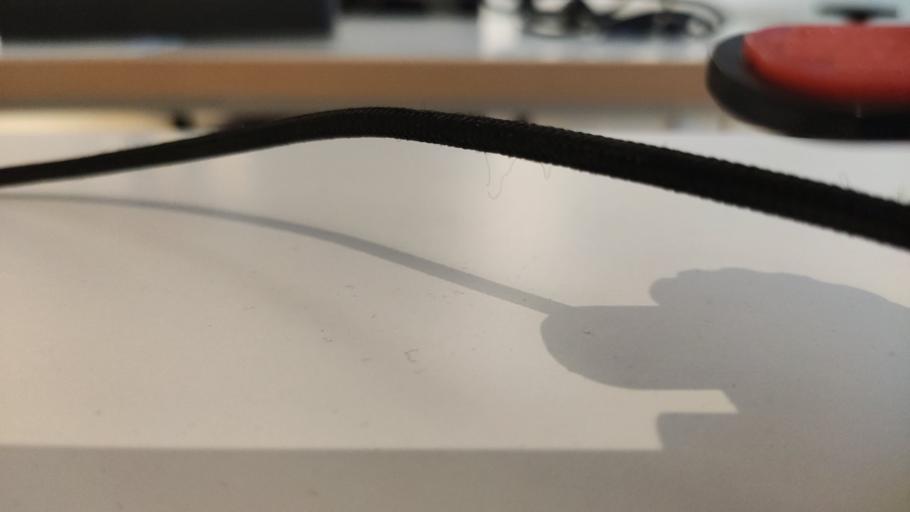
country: RU
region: Moskovskaya
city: Ruza
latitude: 55.7859
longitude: 36.2776
